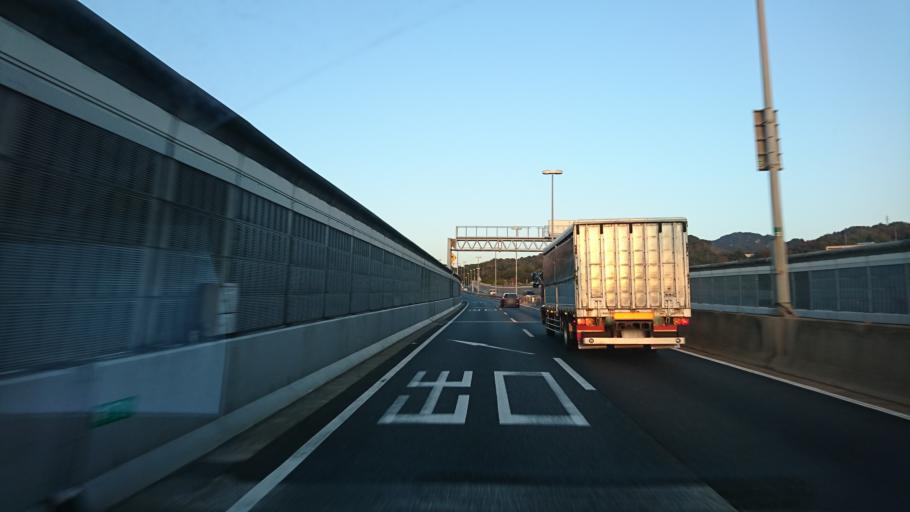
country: JP
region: Hyogo
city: Kobe
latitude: 34.6512
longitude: 135.1262
